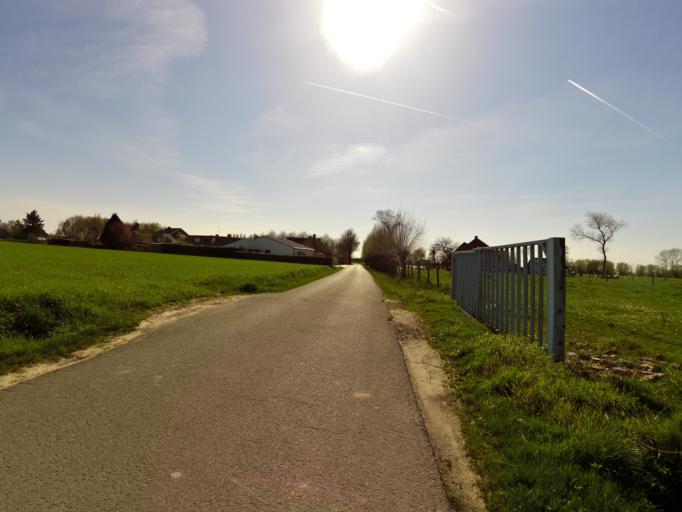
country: BE
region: Flanders
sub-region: Provincie West-Vlaanderen
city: Jabbeke
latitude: 51.1844
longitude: 3.0808
